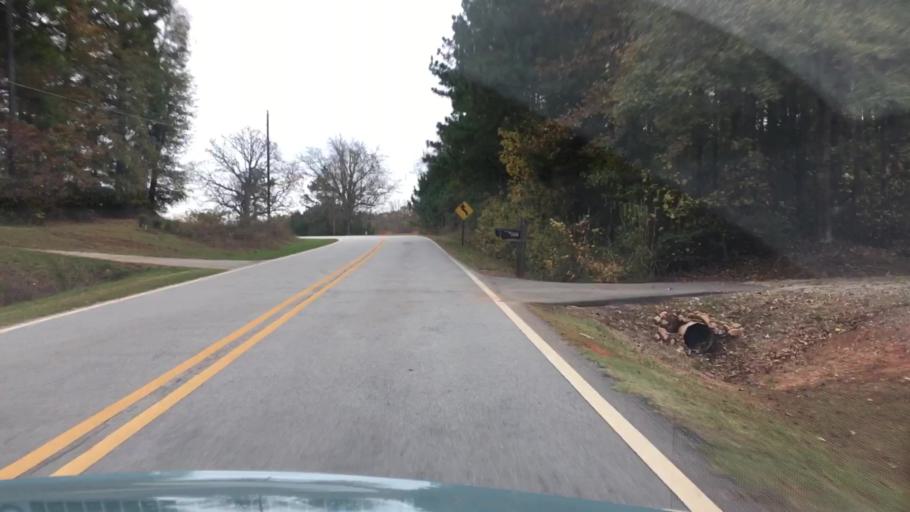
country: US
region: Georgia
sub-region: Henry County
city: McDonough
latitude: 33.5169
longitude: -84.1270
